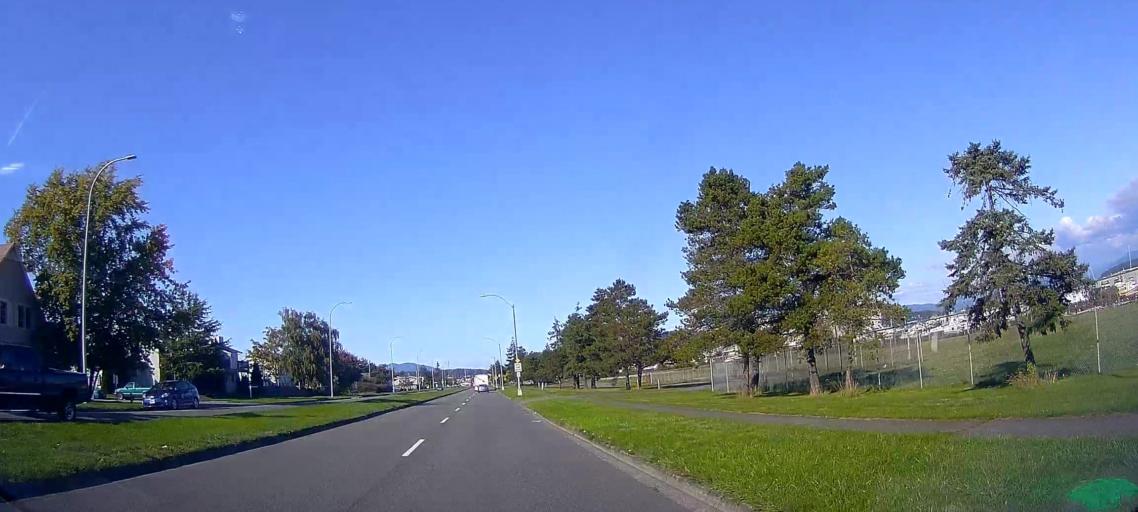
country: US
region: Washington
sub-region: Skagit County
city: Anacortes
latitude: 48.5009
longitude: -122.6095
